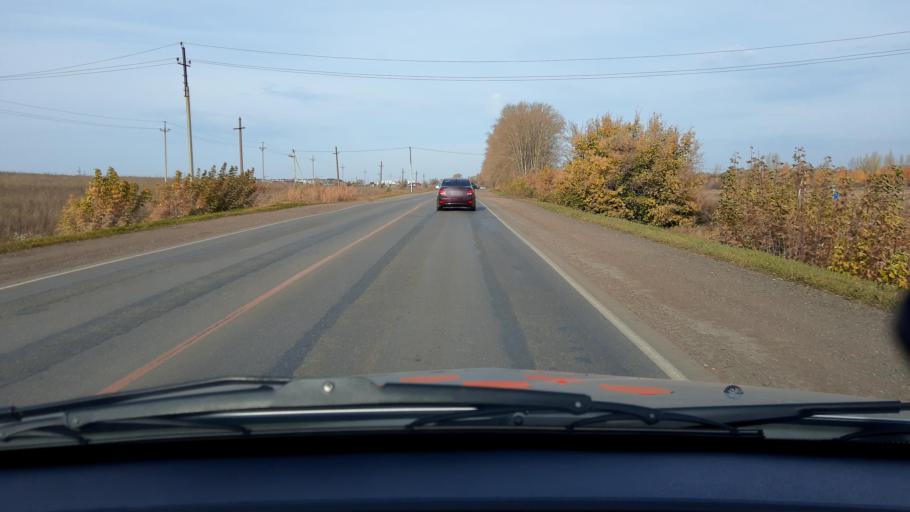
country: RU
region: Bashkortostan
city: Avdon
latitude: 54.7263
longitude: 55.8063
